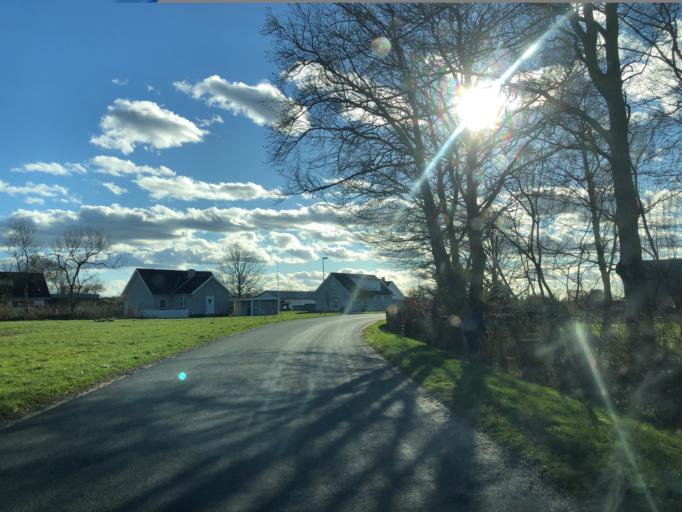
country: DK
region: Central Jutland
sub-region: Silkeborg Kommune
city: Kjellerup
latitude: 56.3332
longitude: 9.4894
